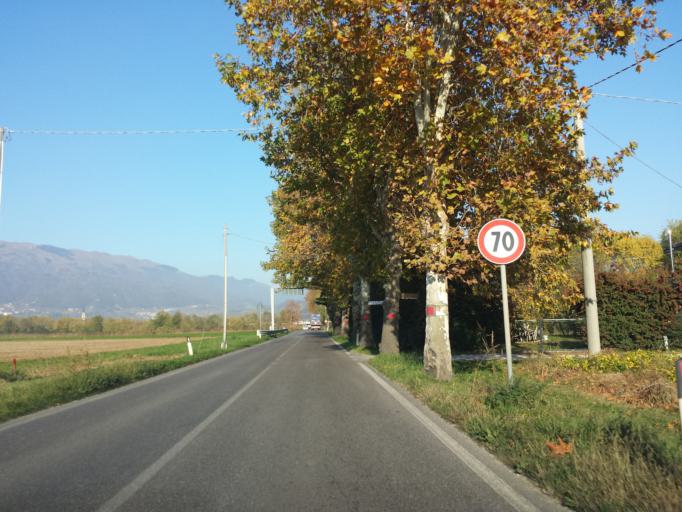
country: IT
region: Veneto
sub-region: Provincia di Treviso
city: Covolo-Levada
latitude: 45.8436
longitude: 12.0170
